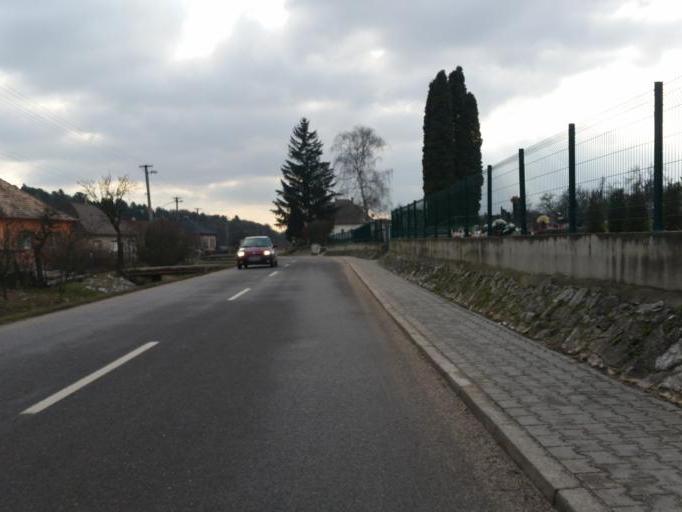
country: SK
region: Trnavsky
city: Vrbove
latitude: 48.6530
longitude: 17.7175
